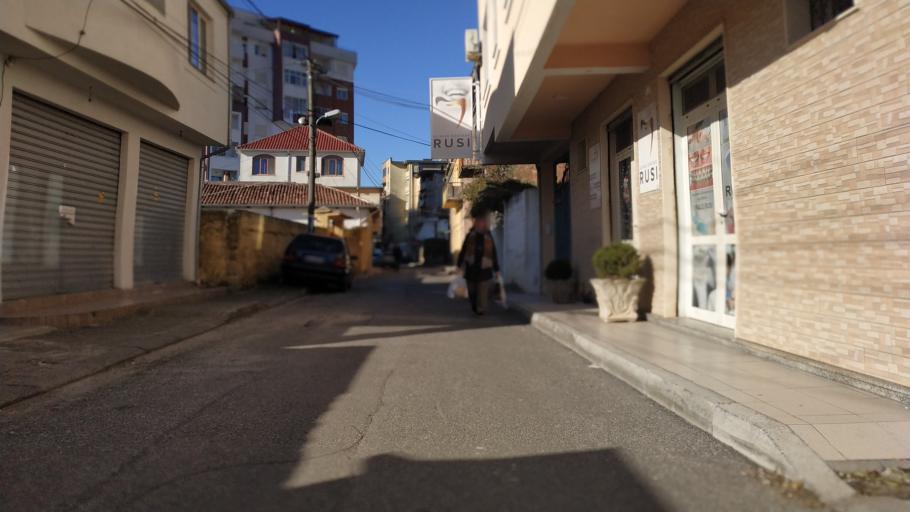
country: AL
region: Shkoder
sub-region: Rrethi i Shkodres
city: Shkoder
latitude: 42.0733
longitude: 19.5171
